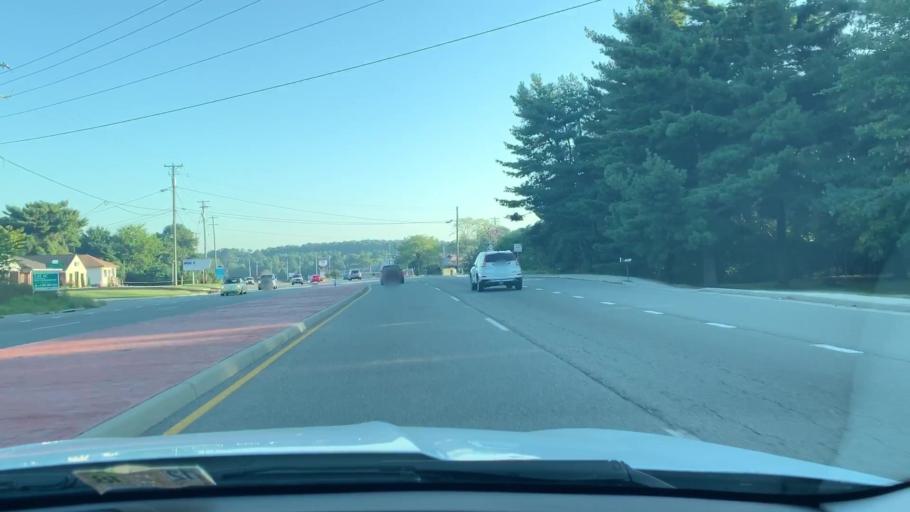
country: US
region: Virginia
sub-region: Gloucester County
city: Gloucester Point
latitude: 37.2574
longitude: -76.4957
